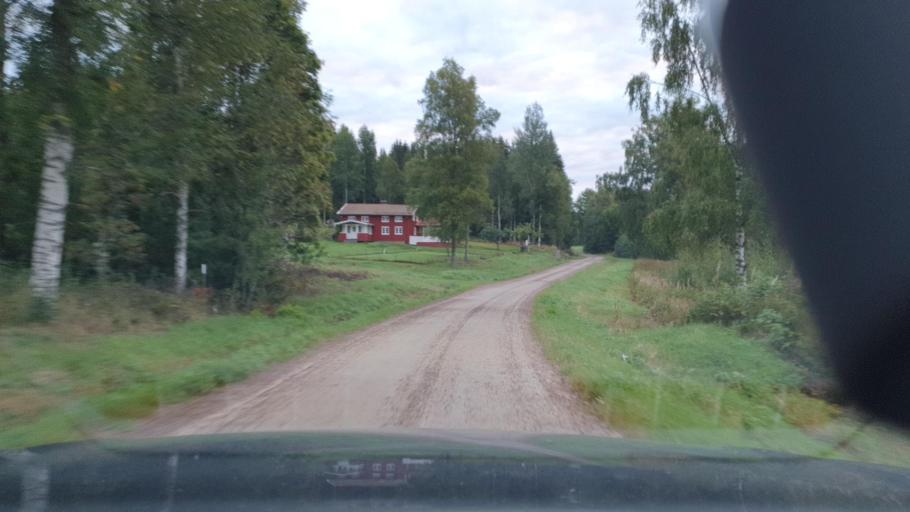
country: SE
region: Vaermland
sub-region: Munkfors Kommun
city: Munkfors
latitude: 59.7939
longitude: 13.4238
